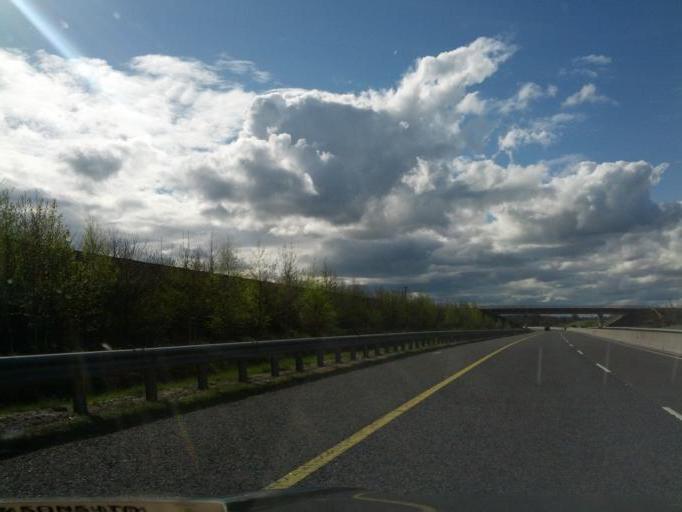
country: IE
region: Leinster
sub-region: Uibh Fhaili
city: Clara
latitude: 53.3884
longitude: -7.6055
